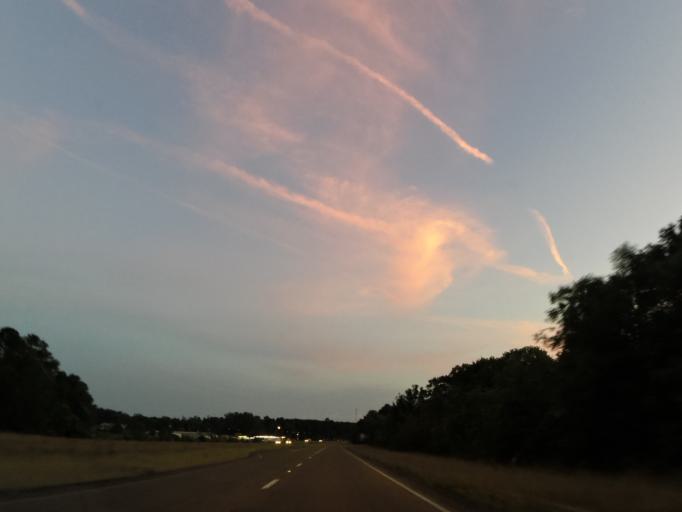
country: US
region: Mississippi
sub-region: Lauderdale County
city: Meridian Station
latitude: 32.5253
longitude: -88.5143
